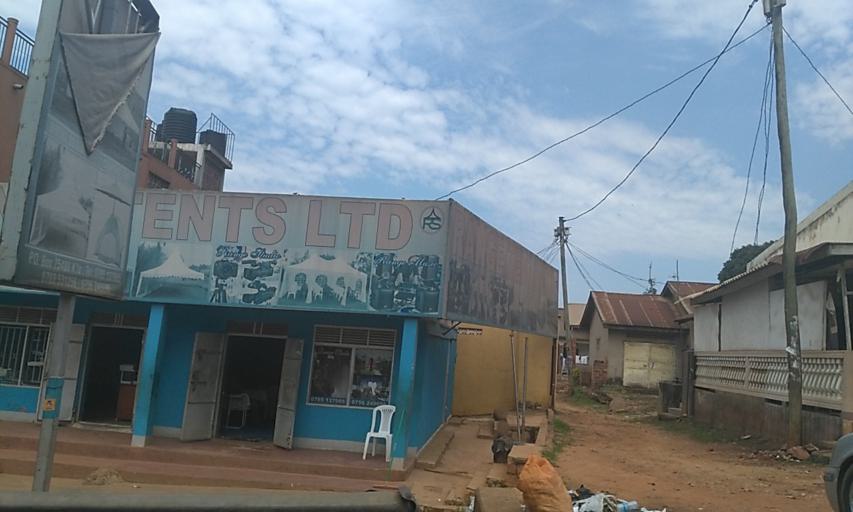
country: UG
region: Central Region
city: Kampala Central Division
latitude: 0.3049
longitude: 32.5475
